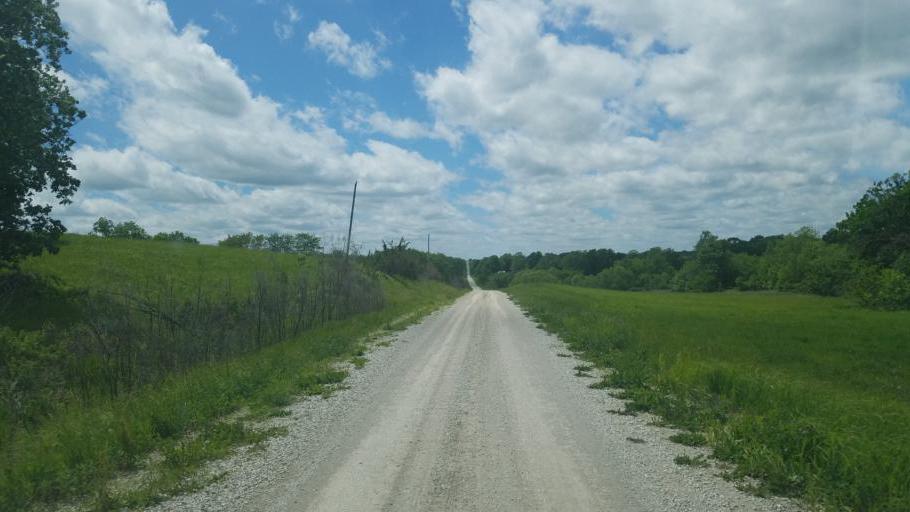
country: US
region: Iowa
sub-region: Decatur County
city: Lamoni
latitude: 40.5005
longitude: -93.9981
